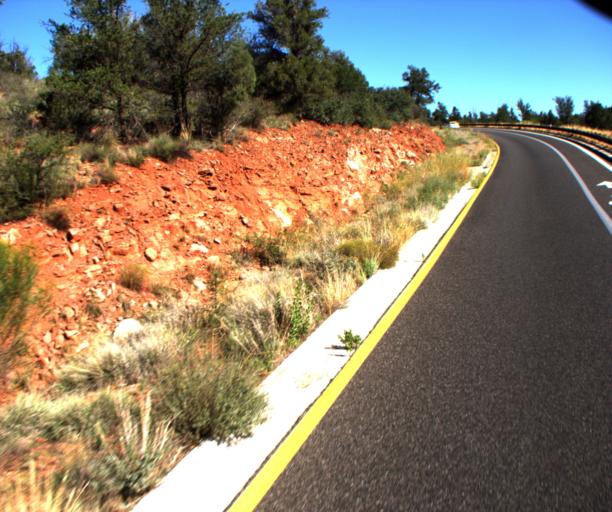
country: US
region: Arizona
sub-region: Yavapai County
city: Village of Oak Creek (Big Park)
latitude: 34.8200
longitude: -111.7724
